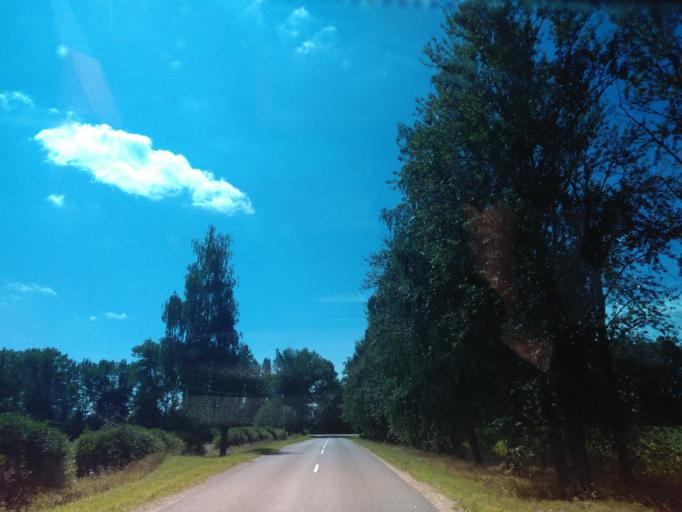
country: BY
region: Minsk
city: Kapyl'
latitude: 53.2470
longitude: 27.1823
